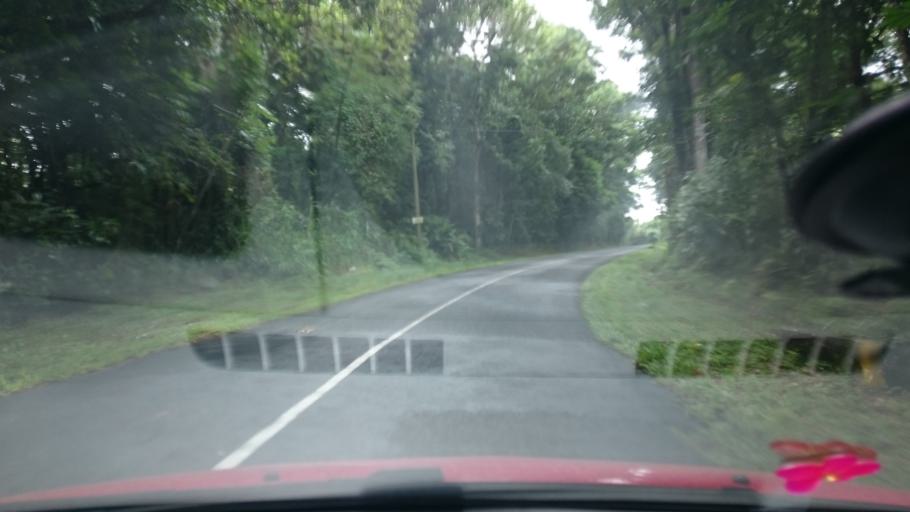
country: MQ
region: Martinique
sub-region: Martinique
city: Riviere-Pilote
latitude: 14.4984
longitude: -60.9264
